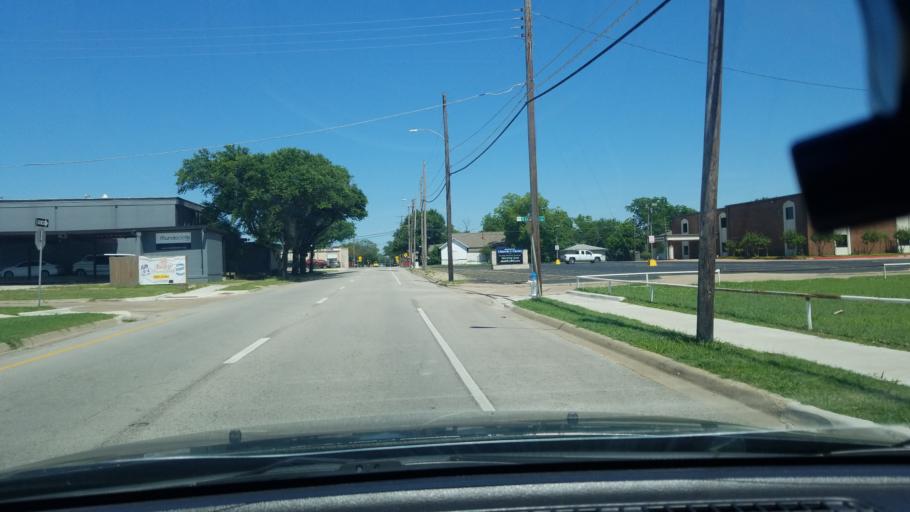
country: US
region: Texas
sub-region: Dallas County
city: Mesquite
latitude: 32.7667
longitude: -96.6037
